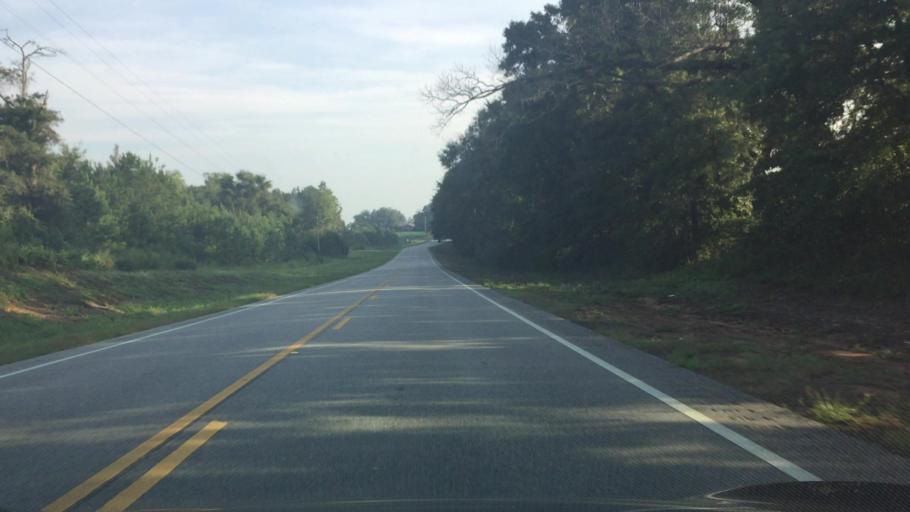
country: US
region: Alabama
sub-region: Covington County
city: Andalusia
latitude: 31.1642
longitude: -86.4596
